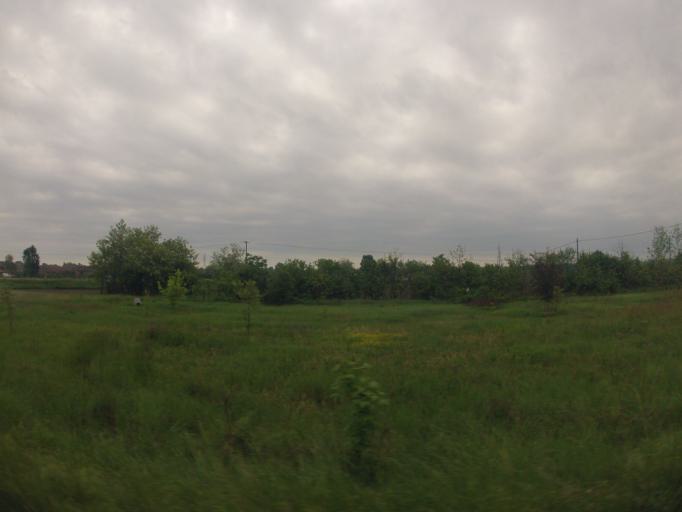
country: IT
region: Piedmont
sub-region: Provincia di Torino
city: Carignano
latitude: 44.8909
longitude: 7.6690
